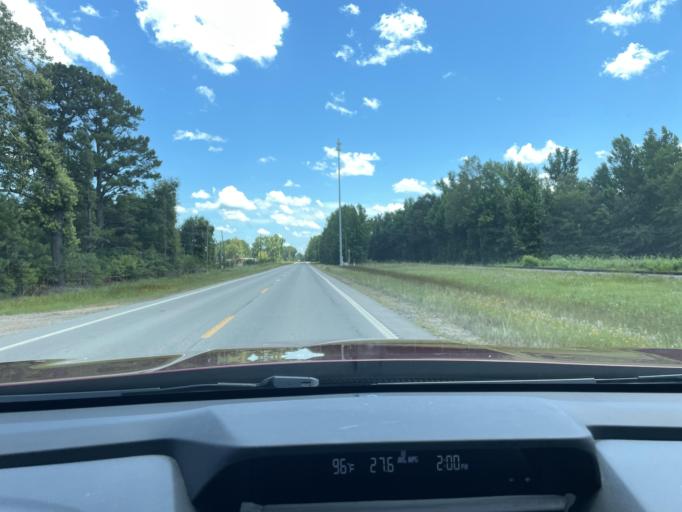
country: US
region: Arkansas
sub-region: Drew County
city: Monticello
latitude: 33.6139
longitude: -91.7426
